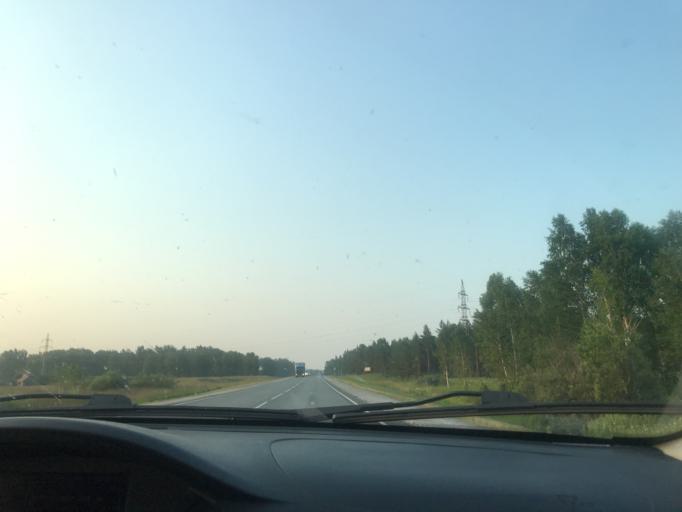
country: RU
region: Novosibirsk
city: Dorogino
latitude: 54.3756
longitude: 83.3056
